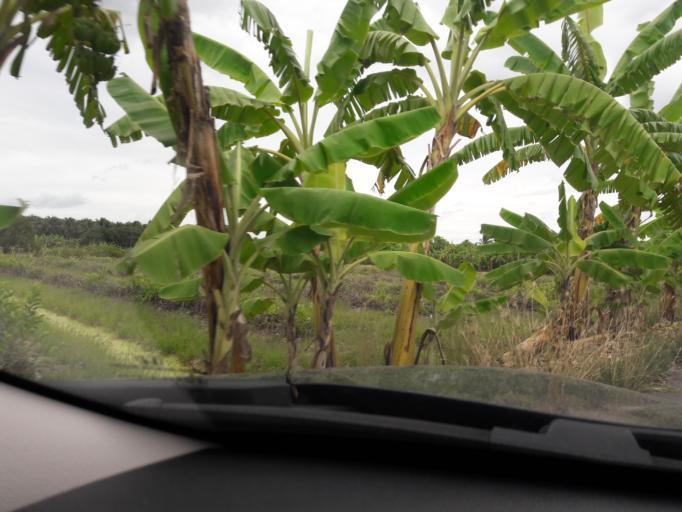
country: TH
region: Ratchaburi
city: Bang Phae
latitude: 13.6269
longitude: 99.9554
